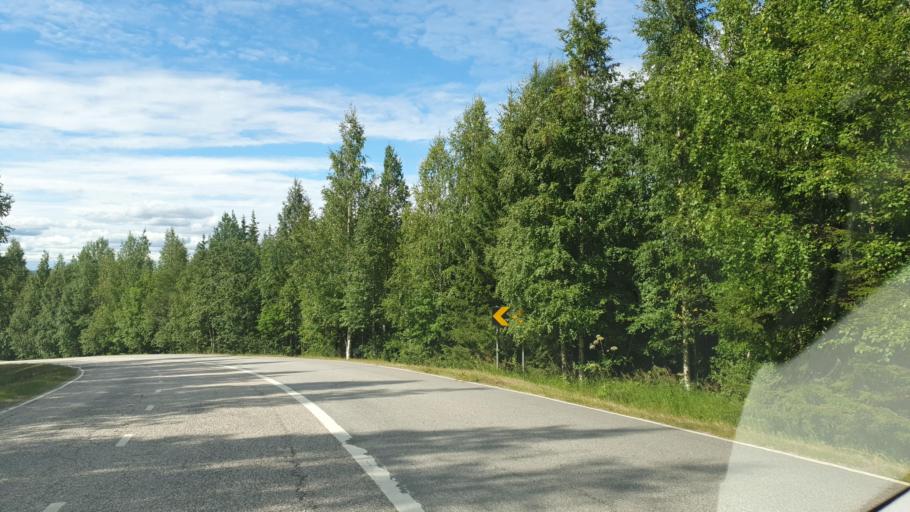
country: FI
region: Kainuu
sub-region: Kajaani
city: Vuokatti
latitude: 64.1305
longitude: 28.2509
